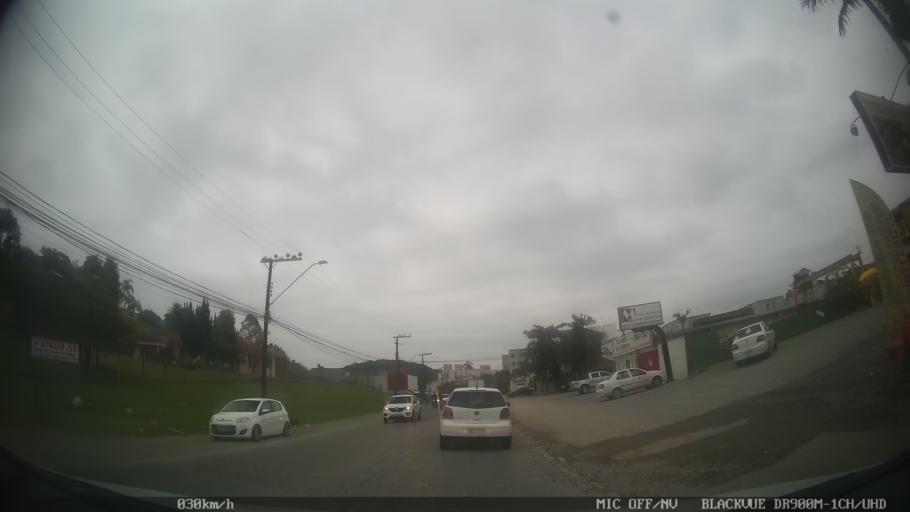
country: BR
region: Santa Catarina
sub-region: Joinville
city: Joinville
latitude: -26.3654
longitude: -48.8371
